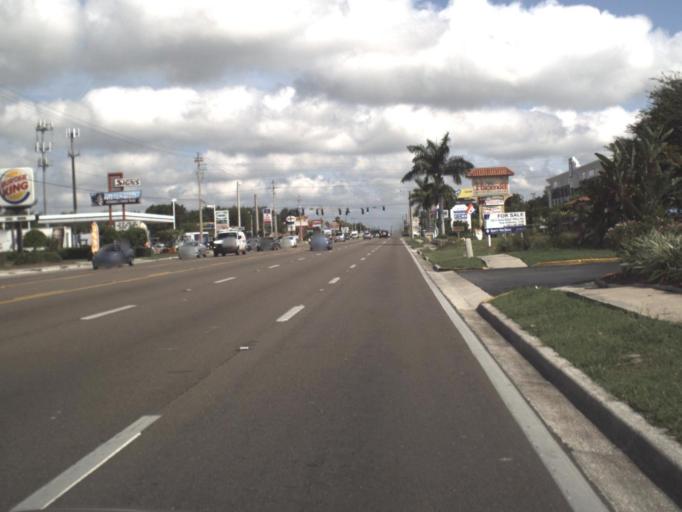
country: US
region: Florida
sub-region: Manatee County
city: Whitfield
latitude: 27.4210
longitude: -82.5754
